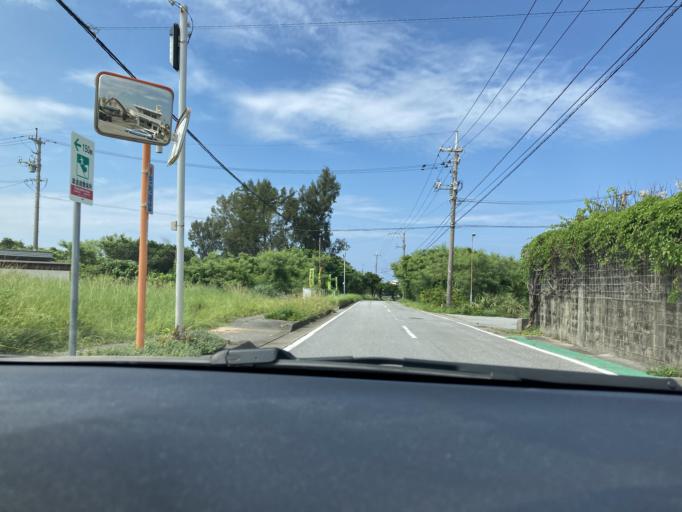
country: JP
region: Okinawa
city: Ishikawa
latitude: 26.4355
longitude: 127.7763
